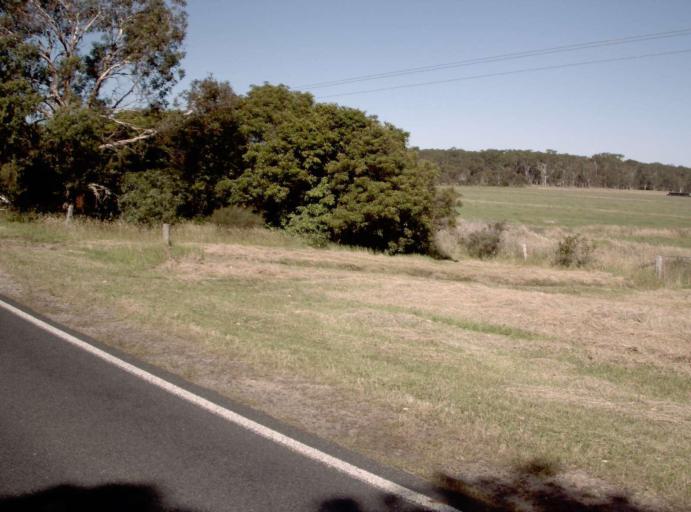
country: AU
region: Victoria
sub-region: Latrobe
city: Morwell
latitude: -38.6511
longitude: 146.4666
